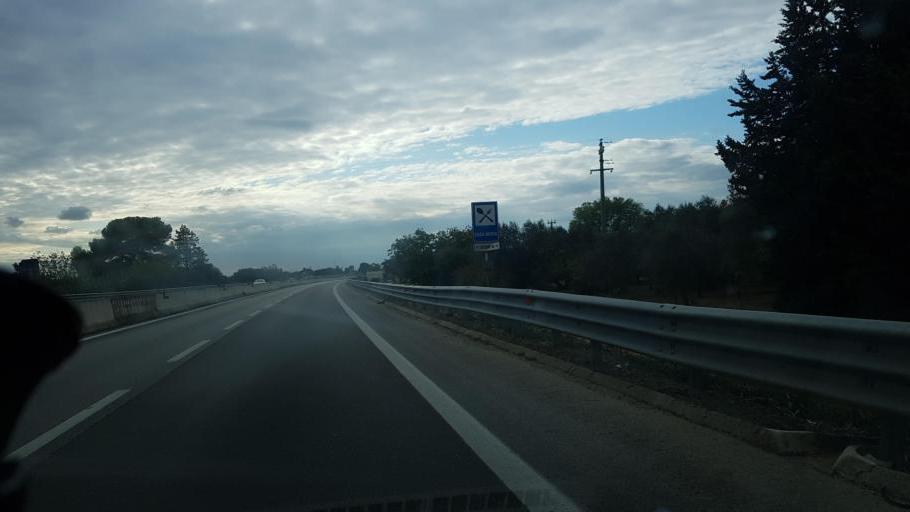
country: IT
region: Apulia
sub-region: Provincia di Brindisi
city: Latiano
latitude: 40.5612
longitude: 17.7319
